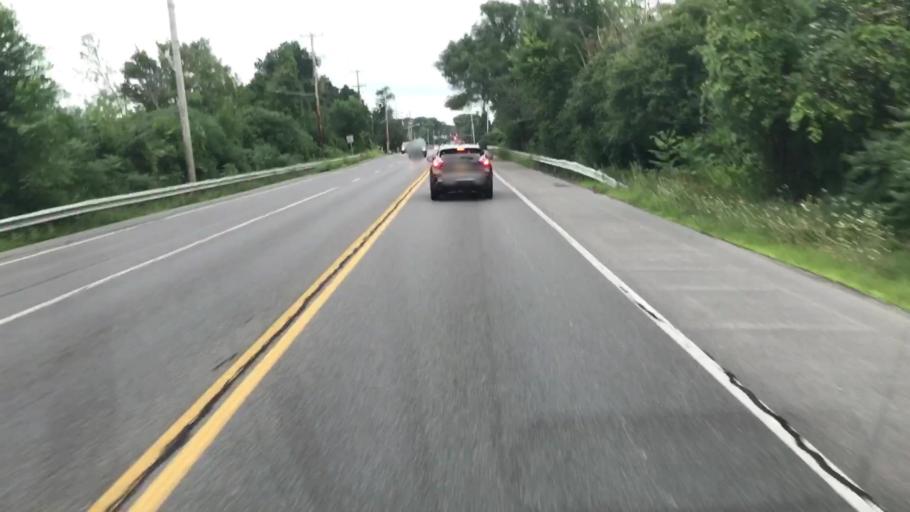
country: US
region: New York
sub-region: Onondaga County
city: North Syracuse
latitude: 43.1394
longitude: -76.1747
